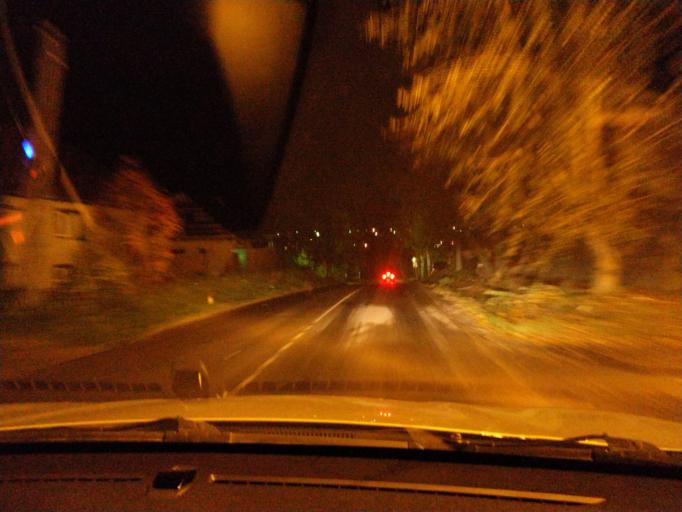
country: RU
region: Perm
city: Dobryanka
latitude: 58.4658
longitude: 56.4185
